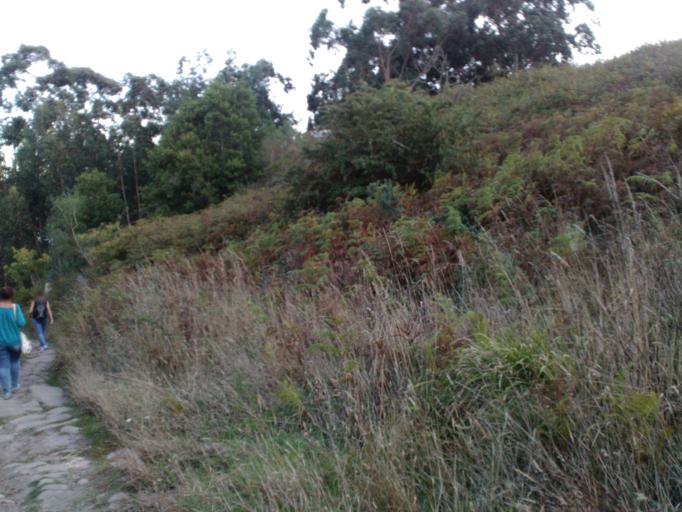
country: ES
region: Galicia
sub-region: Provincia de Pontevedra
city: Cangas
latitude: 42.2766
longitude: -8.8596
